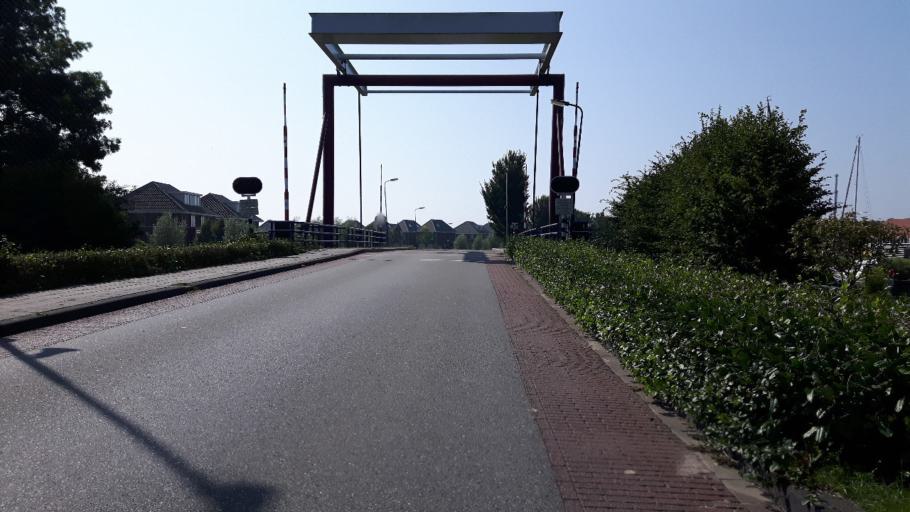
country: NL
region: Friesland
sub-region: Sudwest Fryslan
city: Workum
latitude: 52.9737
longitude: 5.4406
